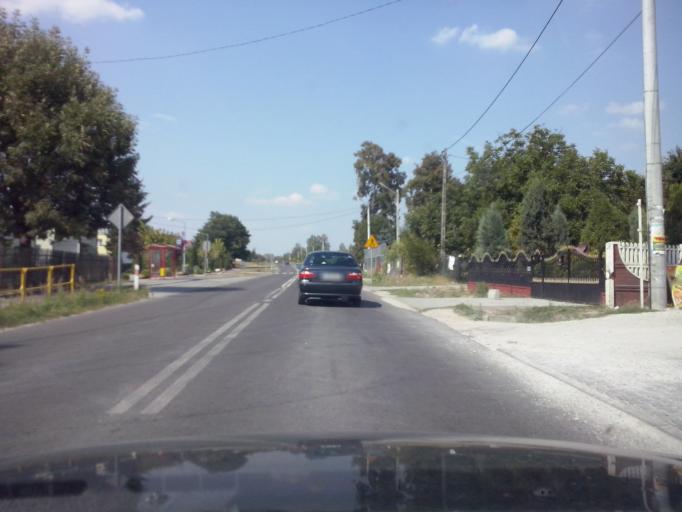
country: PL
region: Swietokrzyskie
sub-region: Powiat buski
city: Gnojno
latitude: 50.6026
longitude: 20.8460
